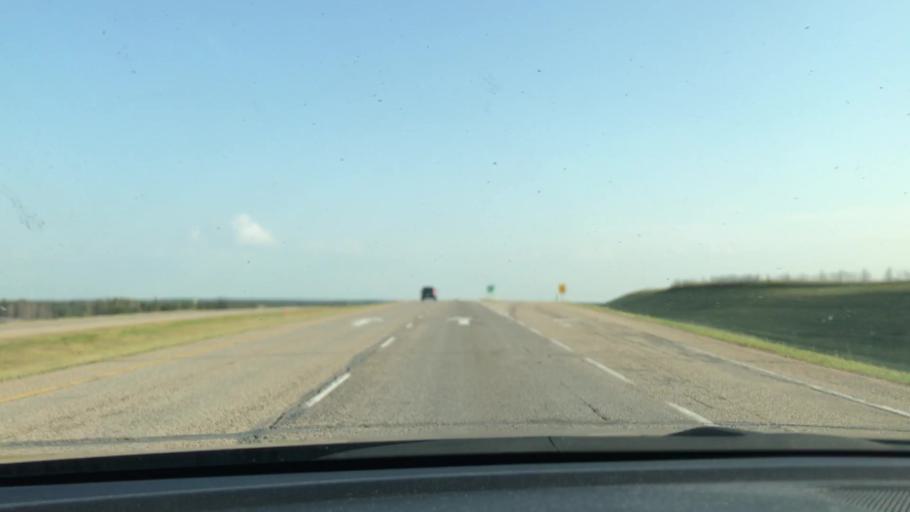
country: CA
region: Alberta
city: Ponoka
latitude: 52.5834
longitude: -113.6633
